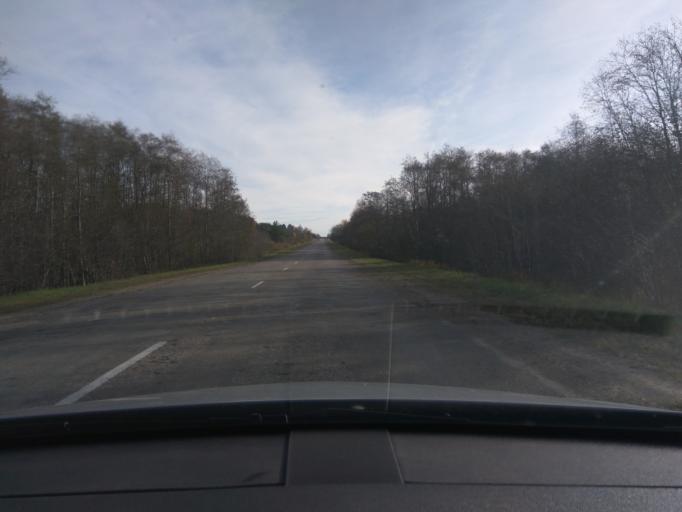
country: LV
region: Alsunga
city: Alsunga
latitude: 57.0044
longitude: 21.7394
